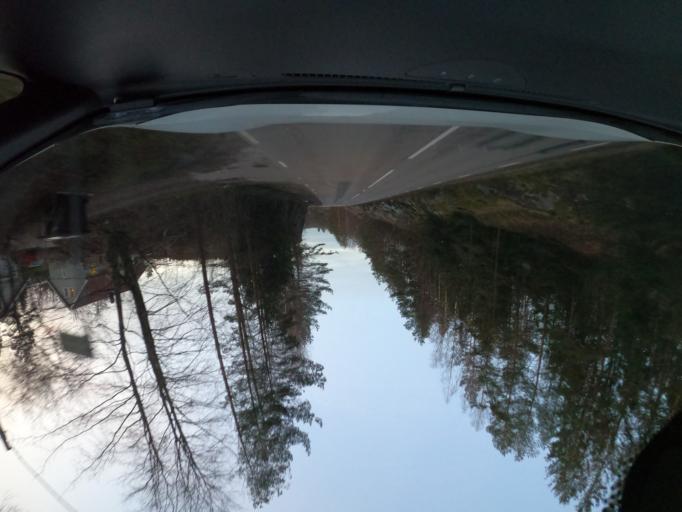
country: SE
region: Vaestra Goetaland
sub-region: Harryda Kommun
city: Molnlycke
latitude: 57.6101
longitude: 12.1795
